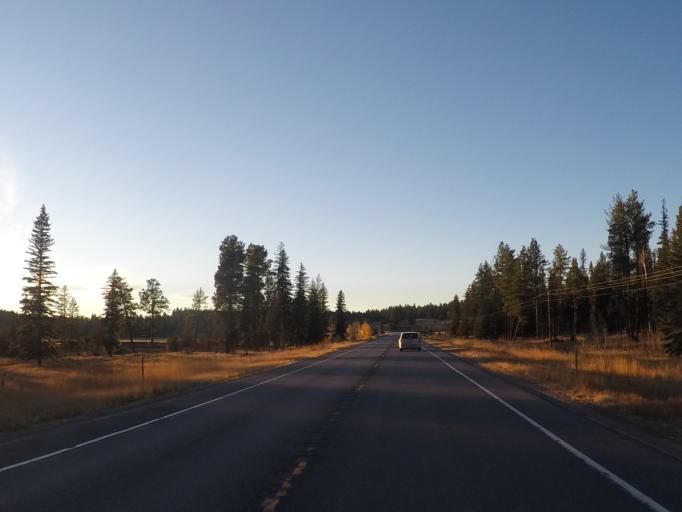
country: US
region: Montana
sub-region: Lewis and Clark County
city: Lincoln
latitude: 47.0033
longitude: -113.0423
